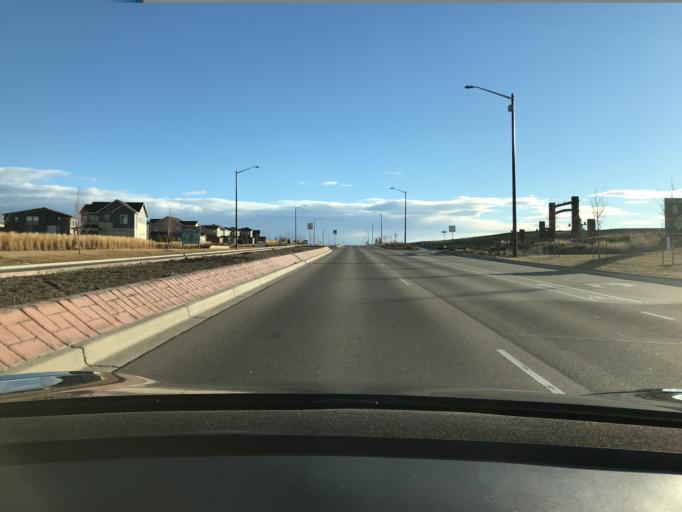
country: US
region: Colorado
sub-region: Boulder County
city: Erie
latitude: 40.0437
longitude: -105.0290
